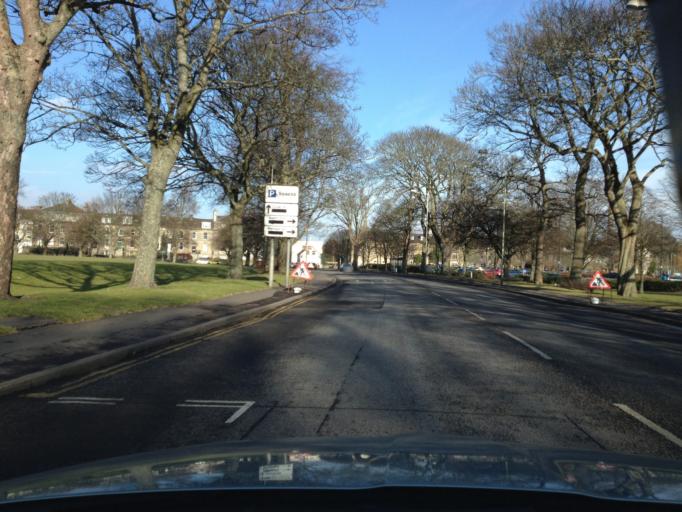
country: GB
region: Scotland
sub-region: Perth and Kinross
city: Perth
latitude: 56.3904
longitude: -3.4290
